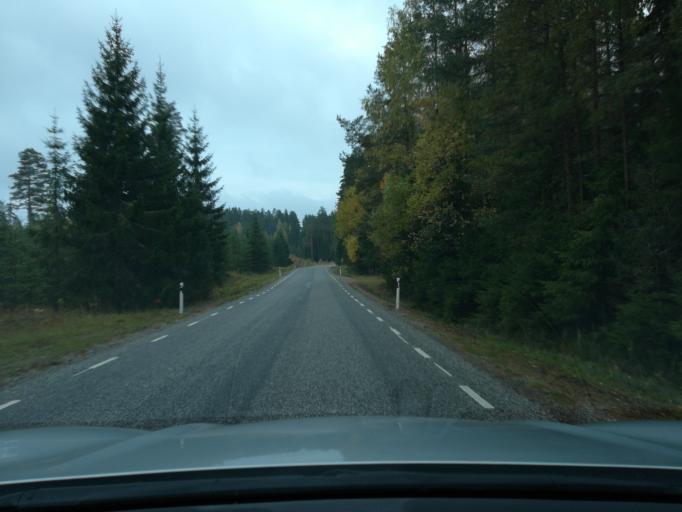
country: EE
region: Ida-Virumaa
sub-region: Johvi vald
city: Johvi
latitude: 59.1788
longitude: 27.4575
